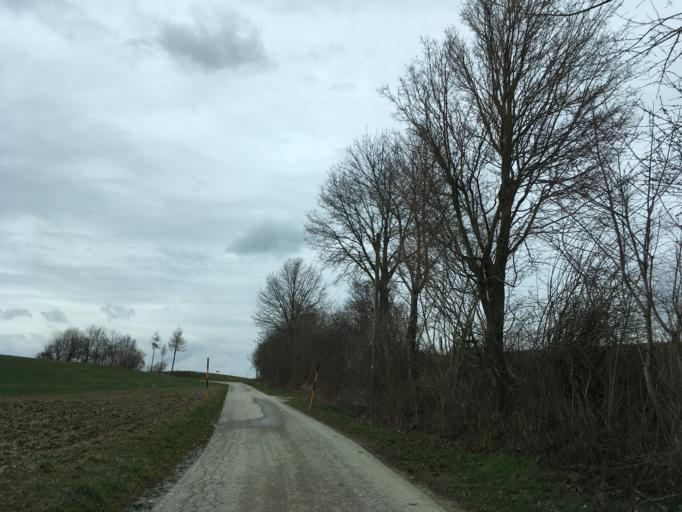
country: DE
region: Bavaria
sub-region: Upper Bavaria
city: Oberbergkirchen
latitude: 48.2668
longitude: 12.3602
